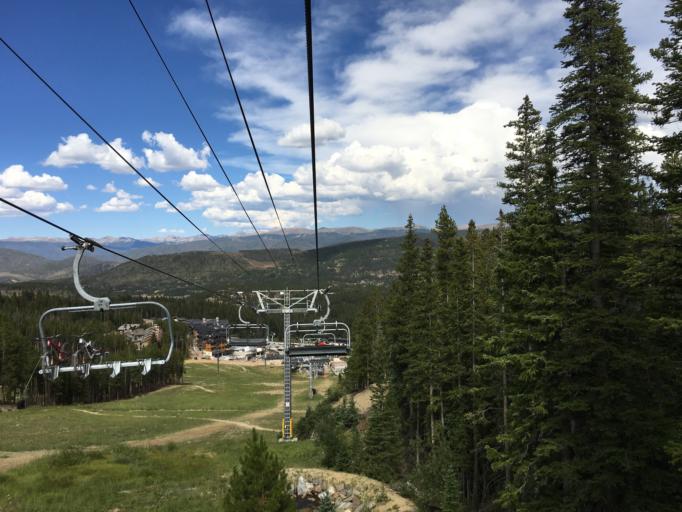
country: US
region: Colorado
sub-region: Summit County
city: Breckenridge
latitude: 39.4785
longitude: -106.0719
